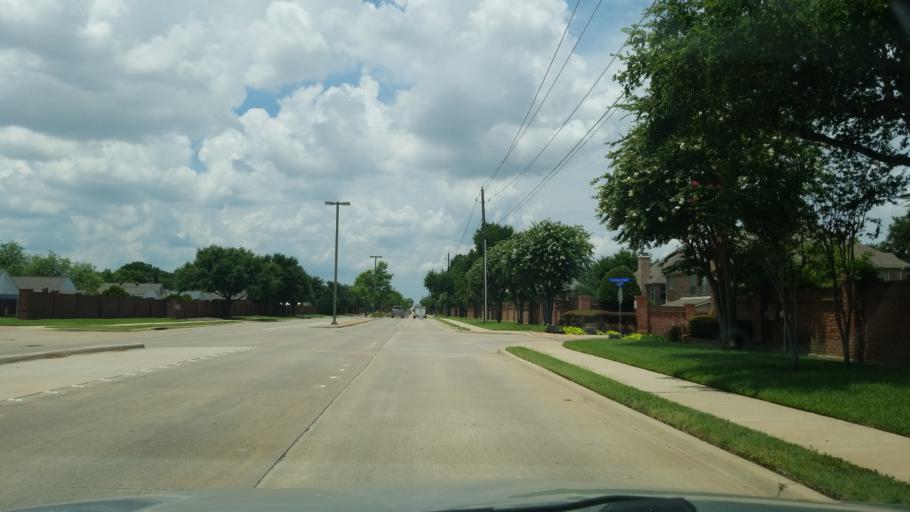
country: US
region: Texas
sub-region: Dallas County
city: Coppell
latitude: 32.9695
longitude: -96.9626
